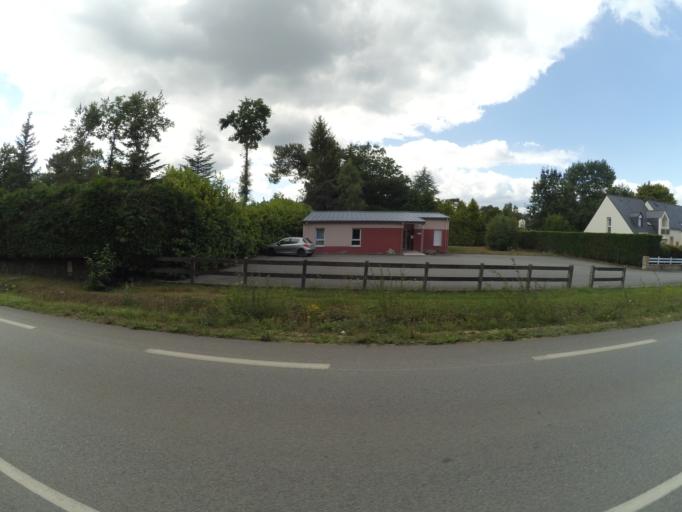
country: FR
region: Brittany
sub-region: Departement du Morbihan
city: Brech
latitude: 47.7147
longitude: -3.0088
